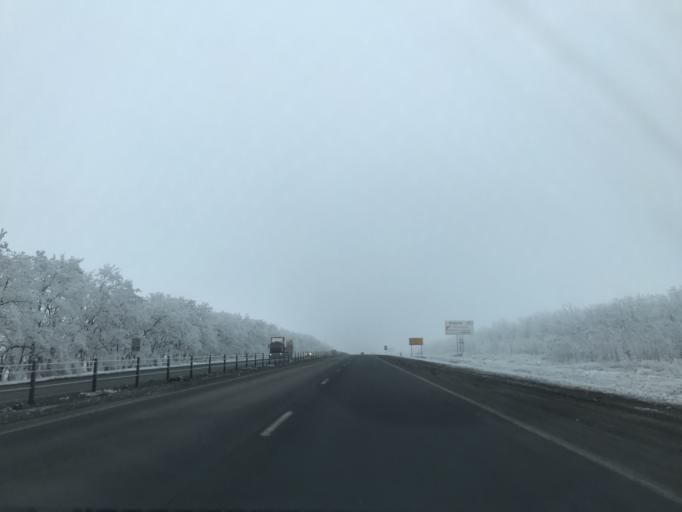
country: RU
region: Rostov
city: Likhoy
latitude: 48.1724
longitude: 40.2640
